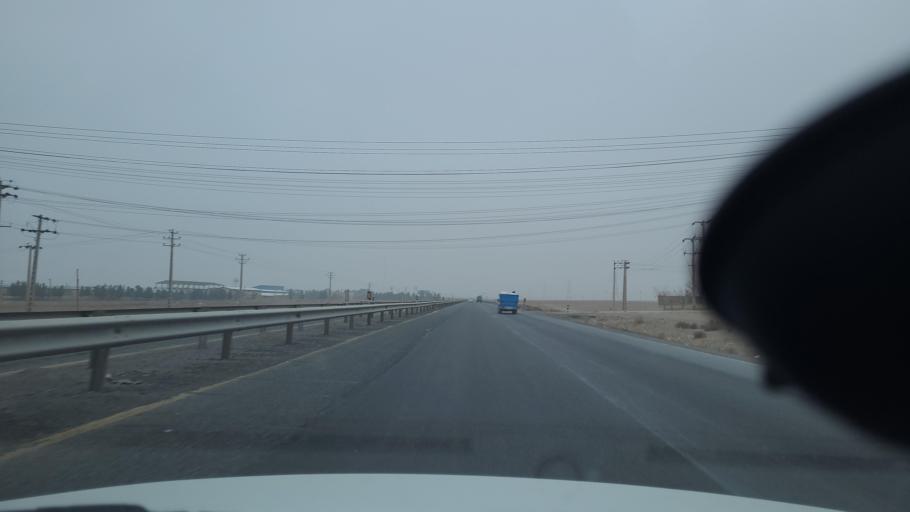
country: IR
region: Razavi Khorasan
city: Fariman
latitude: 35.9128
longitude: 59.7551
